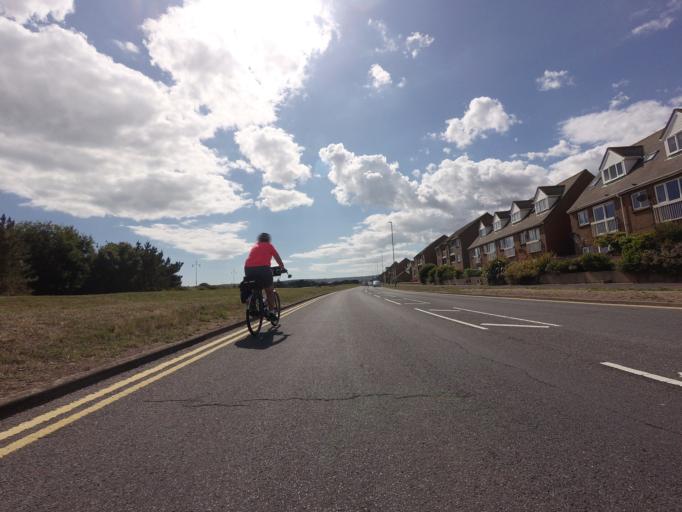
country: GB
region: England
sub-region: East Sussex
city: Pevensey
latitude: 50.7843
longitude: 0.3238
